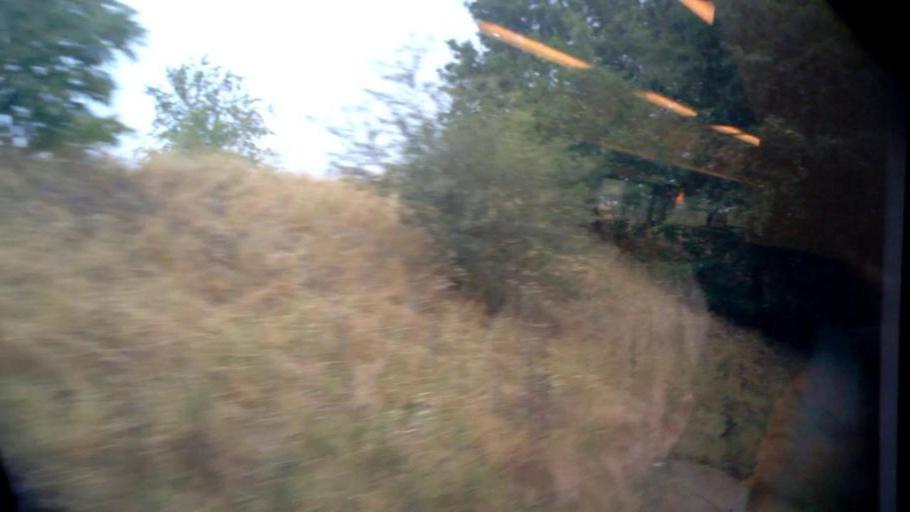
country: DE
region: Brandenburg
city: Grossbeeren
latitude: 52.3444
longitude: 13.2707
